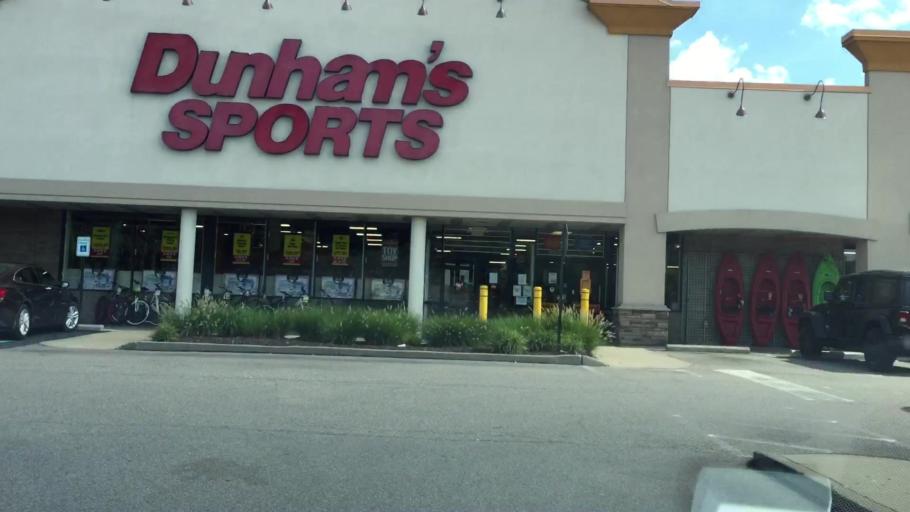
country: US
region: Pennsylvania
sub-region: Allegheny County
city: Bridgeville
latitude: 40.3662
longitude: -80.1088
